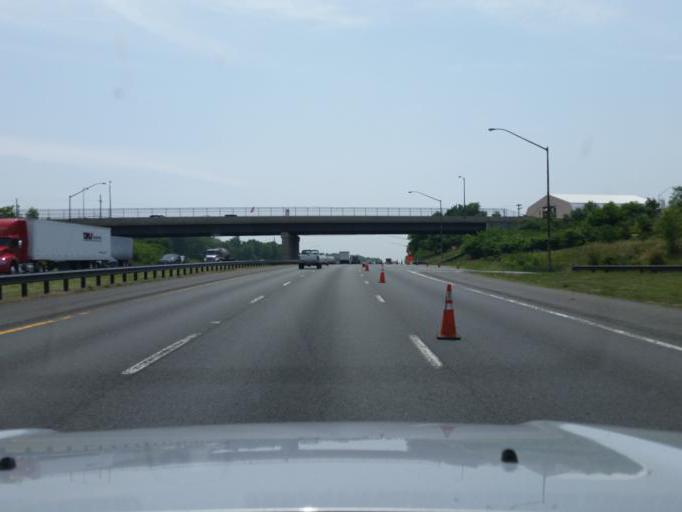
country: US
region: Maryland
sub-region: Montgomery County
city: Clarksburg
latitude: 39.2330
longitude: -77.2859
